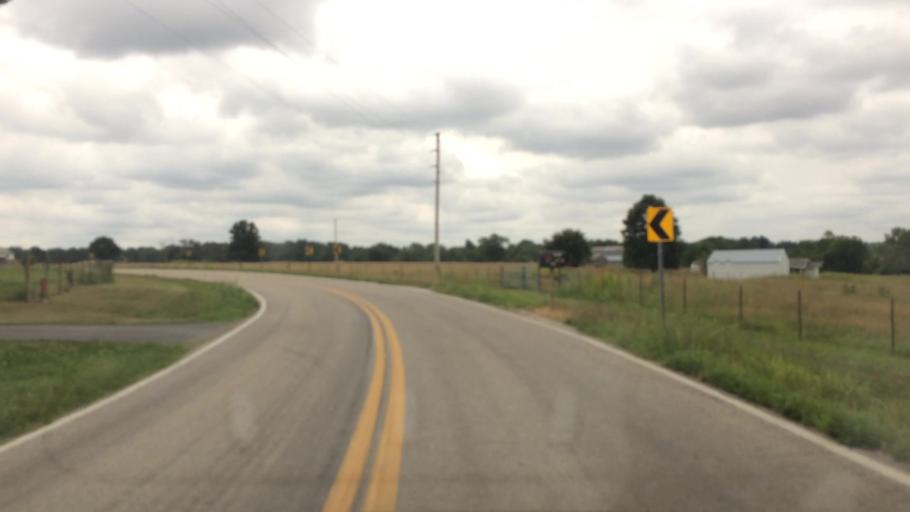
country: US
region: Missouri
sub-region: Greene County
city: Strafford
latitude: 37.2966
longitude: -93.1200
